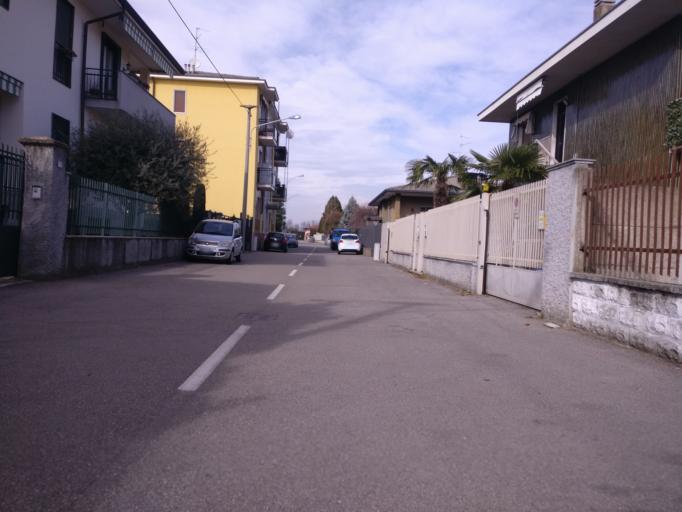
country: IT
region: Lombardy
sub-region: Citta metropolitana di Milano
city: Arluno
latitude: 45.5093
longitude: 8.9368
